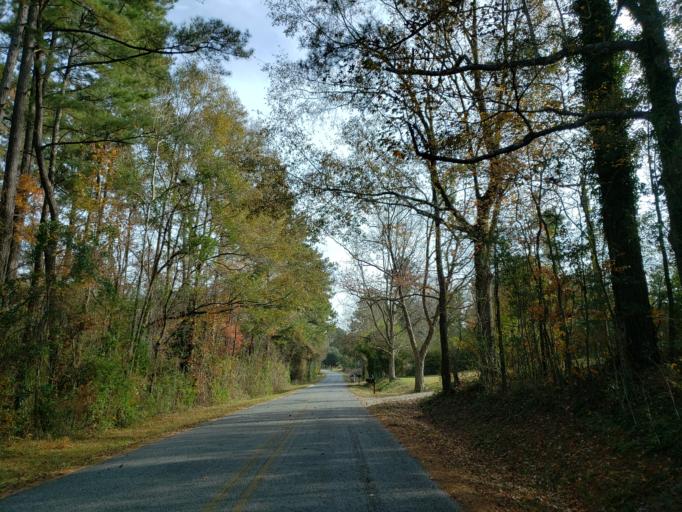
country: US
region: Mississippi
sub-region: Forrest County
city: Rawls Springs
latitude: 31.3745
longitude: -89.3655
